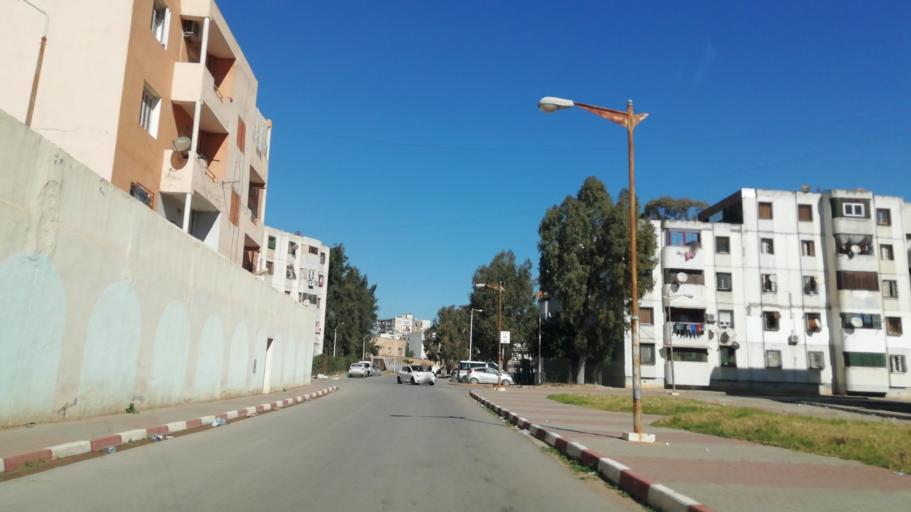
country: DZ
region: Oran
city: Oran
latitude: 35.6873
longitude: -0.6126
